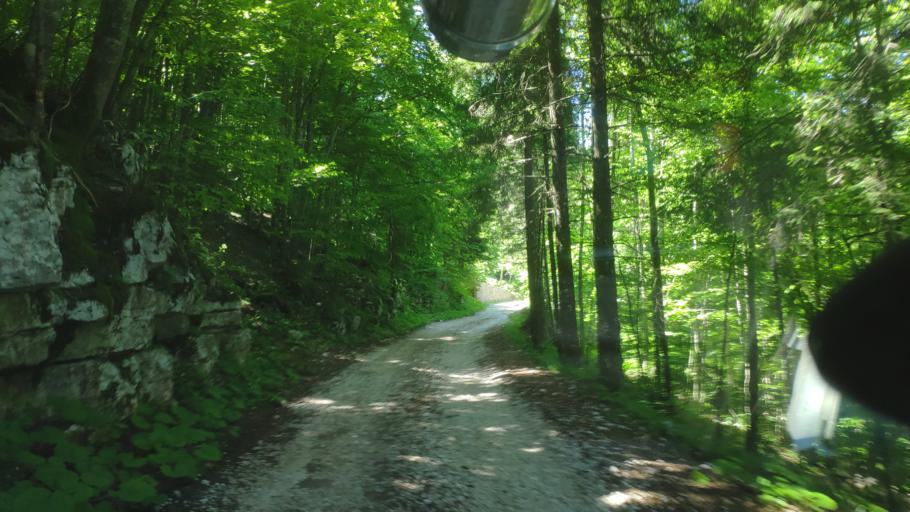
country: IT
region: Veneto
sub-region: Provincia di Vicenza
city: Caltrano
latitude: 45.8123
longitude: 11.4550
